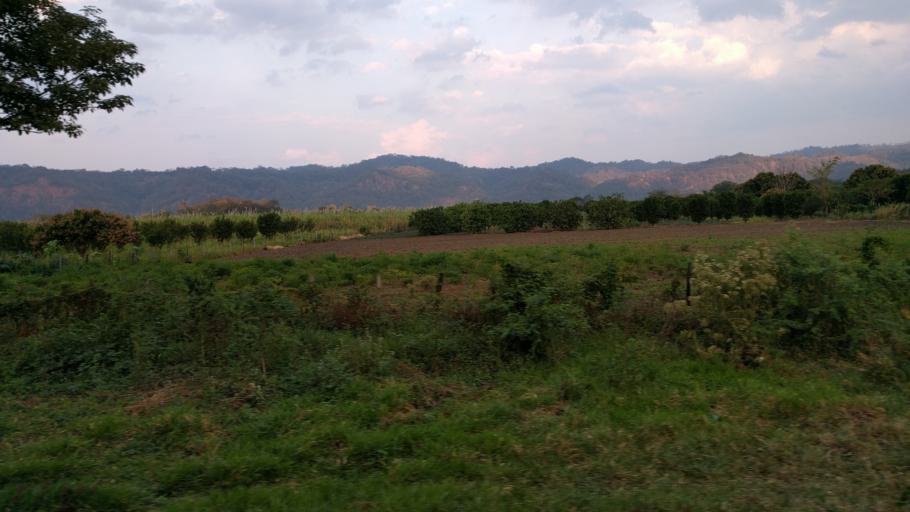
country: BO
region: Santa Cruz
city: Jorochito
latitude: -18.1241
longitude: -63.4644
